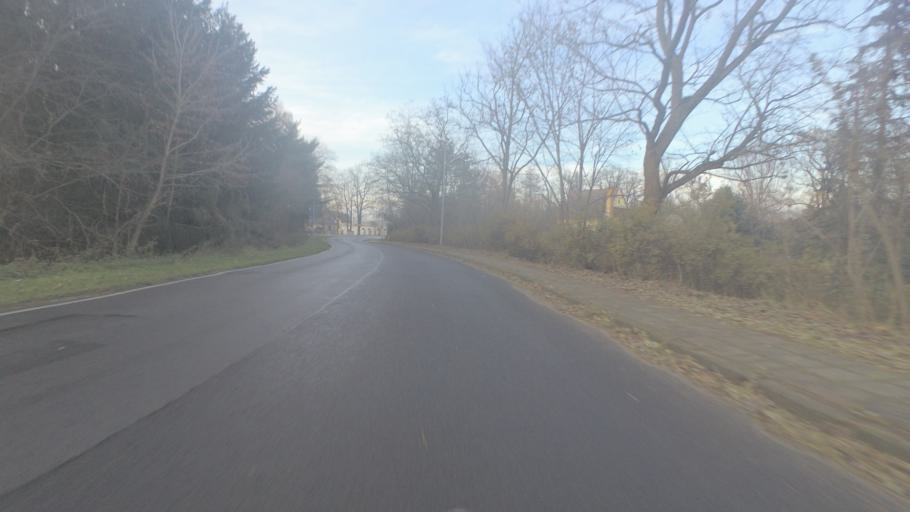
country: DE
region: Brandenburg
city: Am Mellensee
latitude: 52.1801
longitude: 13.3996
